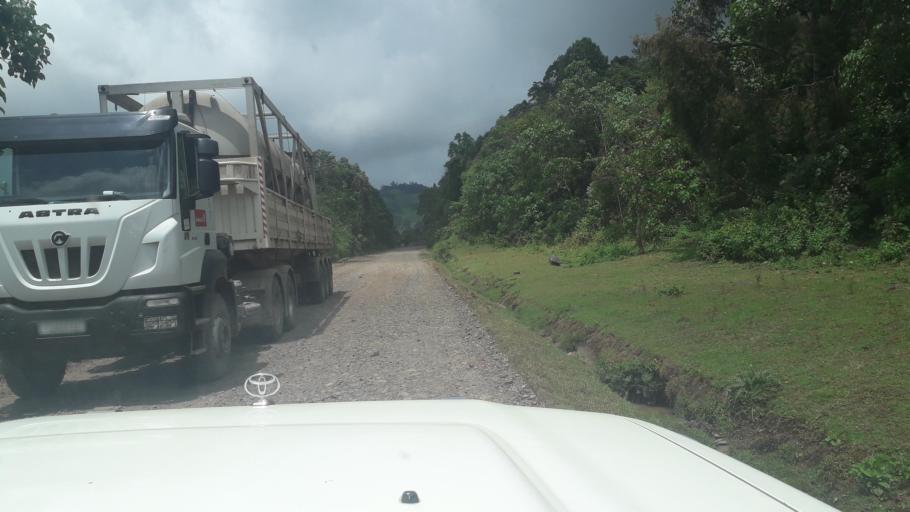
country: ET
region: Oromiya
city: Jima
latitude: 7.4312
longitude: 36.8756
